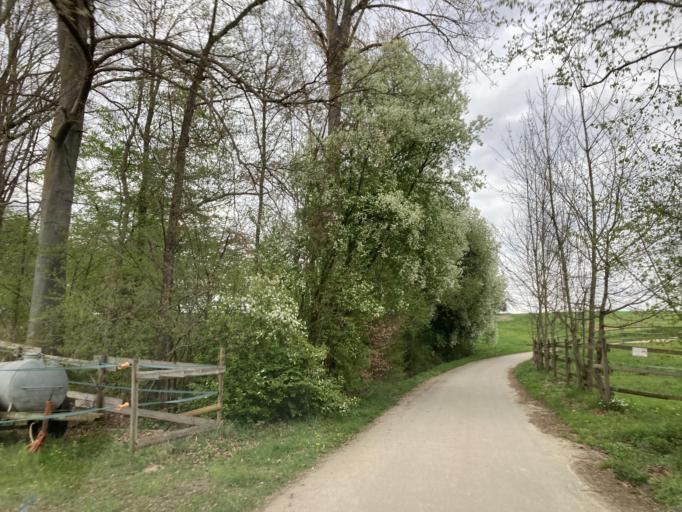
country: DE
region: Baden-Wuerttemberg
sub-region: Tuebingen Region
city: Kusterdingen
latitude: 48.5069
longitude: 9.1310
